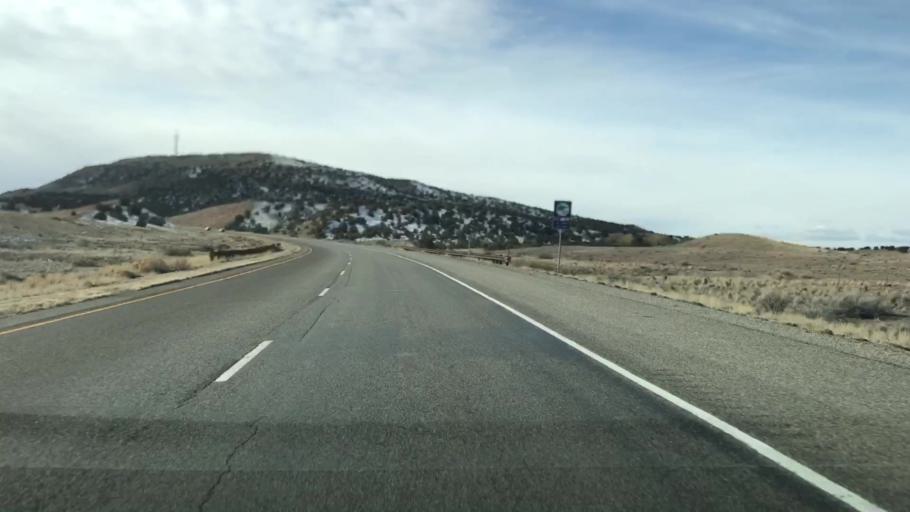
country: US
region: Colorado
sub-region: Mesa County
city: Loma
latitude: 39.2220
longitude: -108.9548
